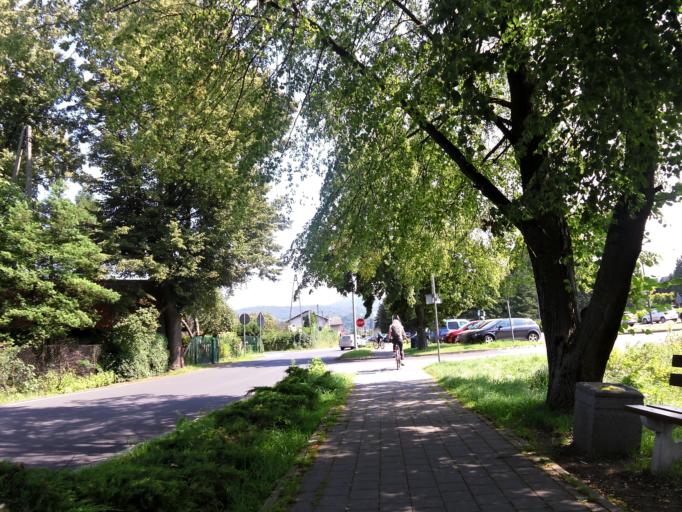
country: PL
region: Silesian Voivodeship
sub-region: Powiat zywiecki
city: Wegierska Gorka
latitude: 49.6149
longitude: 19.1291
